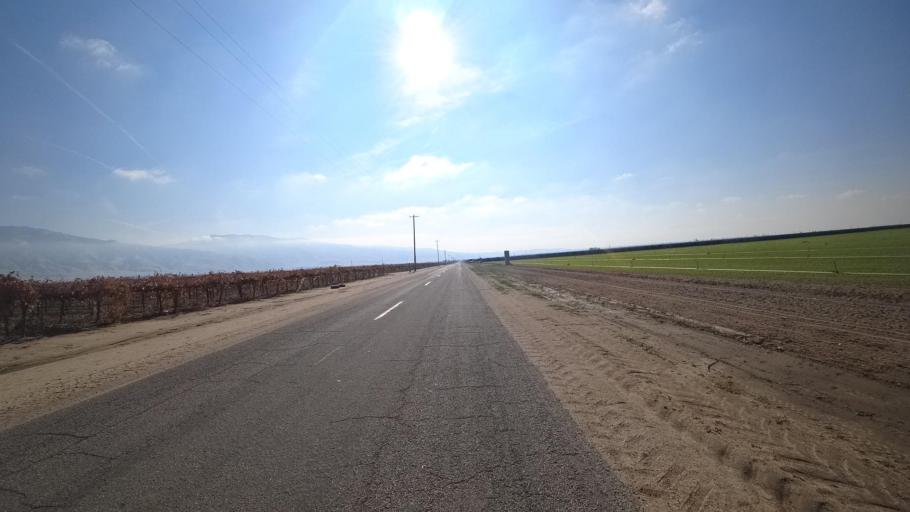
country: US
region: California
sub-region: Kern County
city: Arvin
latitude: 35.2628
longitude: -118.7888
